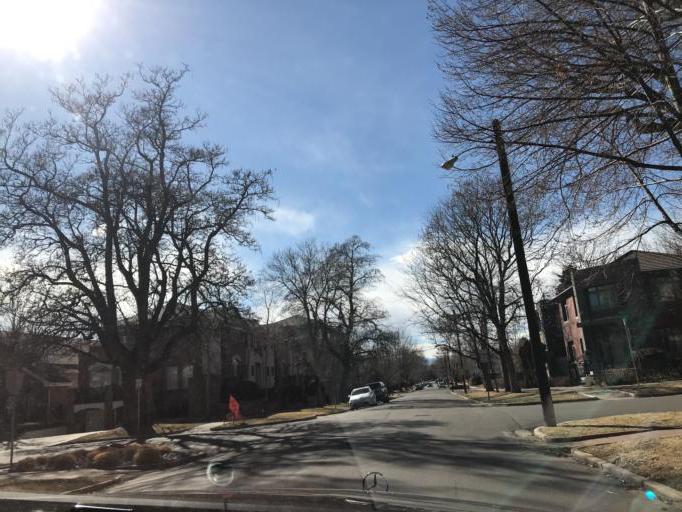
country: US
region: Colorado
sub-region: Arapahoe County
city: Glendale
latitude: 39.7225
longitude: -104.9518
